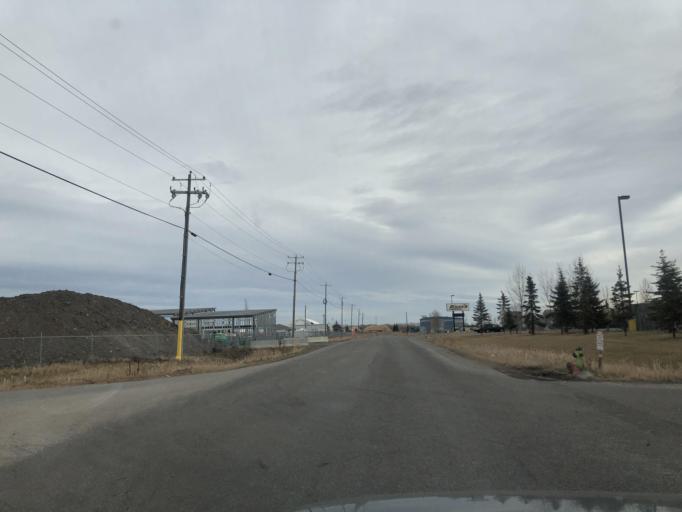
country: CA
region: Alberta
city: Chestermere
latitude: 50.9833
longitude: -113.9064
